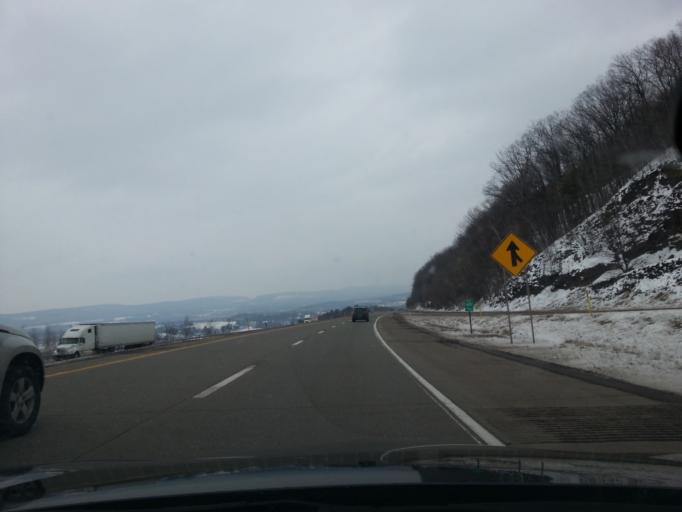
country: US
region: Pennsylvania
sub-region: Luzerne County
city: Conyngham
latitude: 40.9841
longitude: -76.0345
